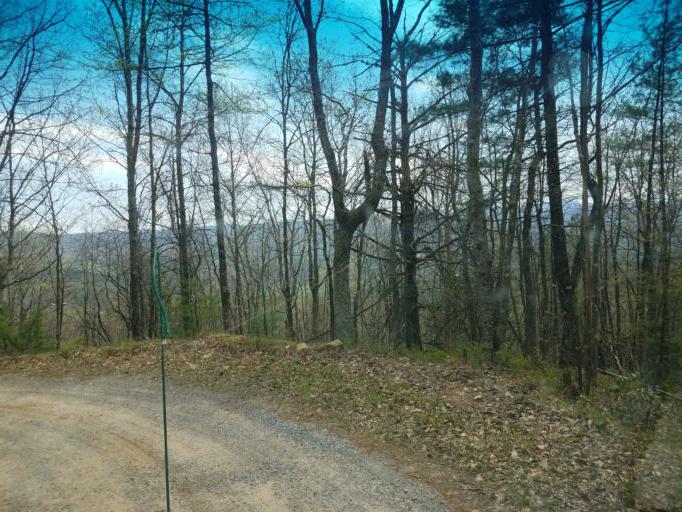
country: US
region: Virginia
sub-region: Smyth County
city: Marion
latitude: 36.7877
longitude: -81.4612
